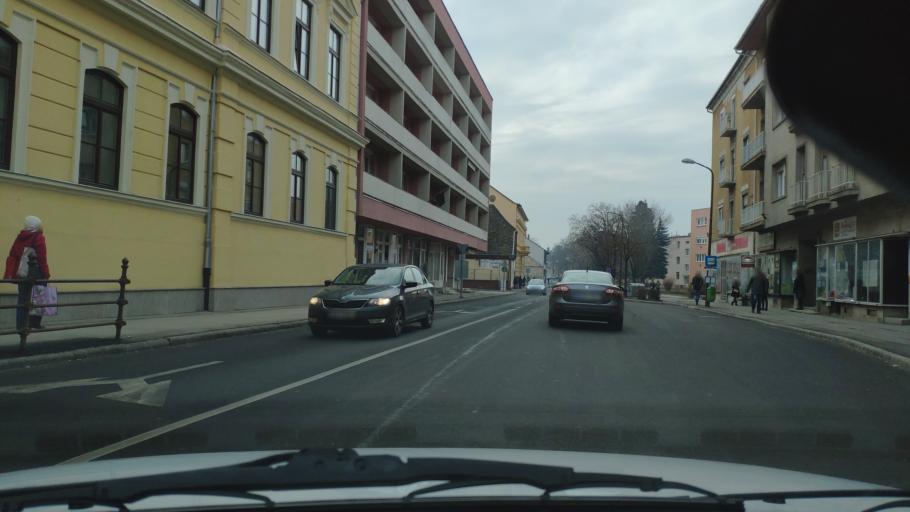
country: HU
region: Zala
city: Nagykanizsa
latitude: 46.4535
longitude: 16.9895
